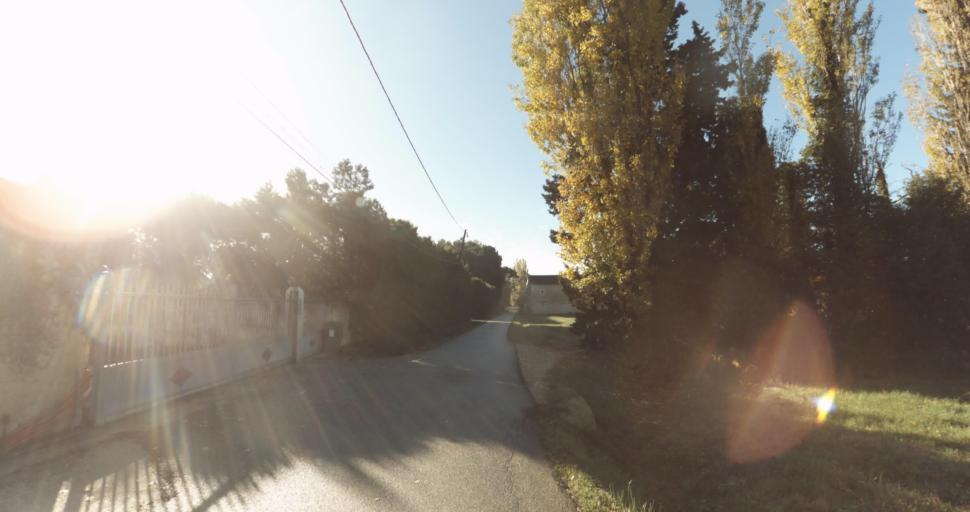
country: FR
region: Provence-Alpes-Cote d'Azur
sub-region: Departement des Bouches-du-Rhone
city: Rognonas
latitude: 43.8838
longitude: 4.8035
